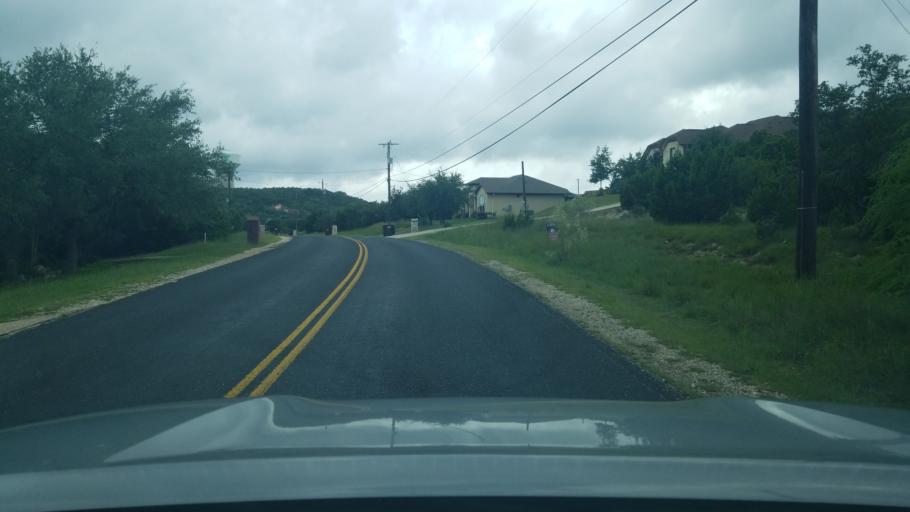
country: US
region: Texas
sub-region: Bexar County
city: Timberwood Park
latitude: 29.6884
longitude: -98.5109
